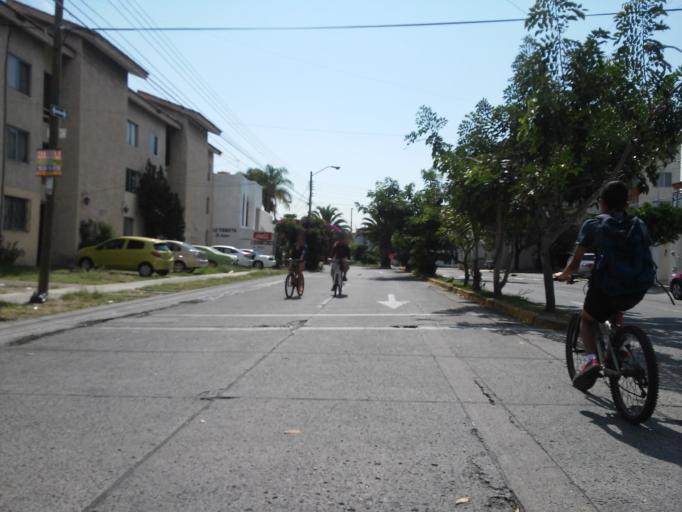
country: MX
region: Jalisco
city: Guadalajara
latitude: 20.6548
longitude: -103.4191
